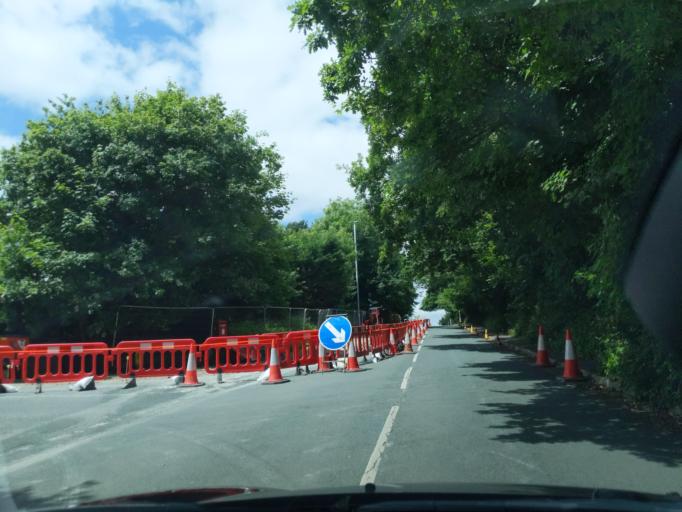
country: GB
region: England
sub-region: Devon
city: Plympton
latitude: 50.4142
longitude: -4.0851
